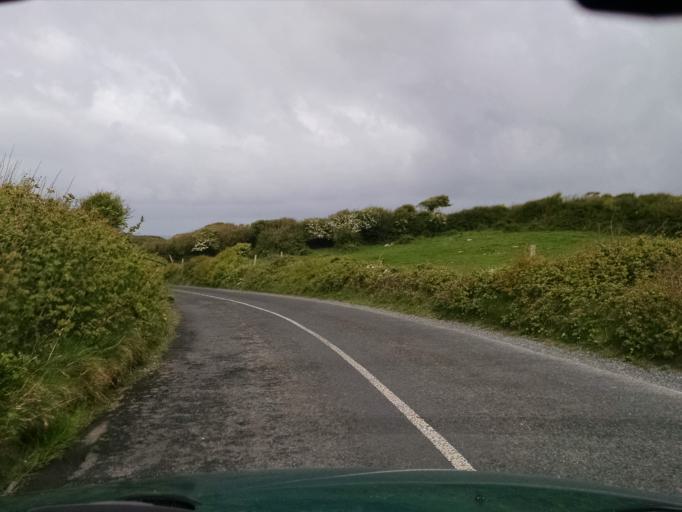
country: IE
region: Connaught
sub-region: County Galway
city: Bearna
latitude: 53.0549
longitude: -9.3498
